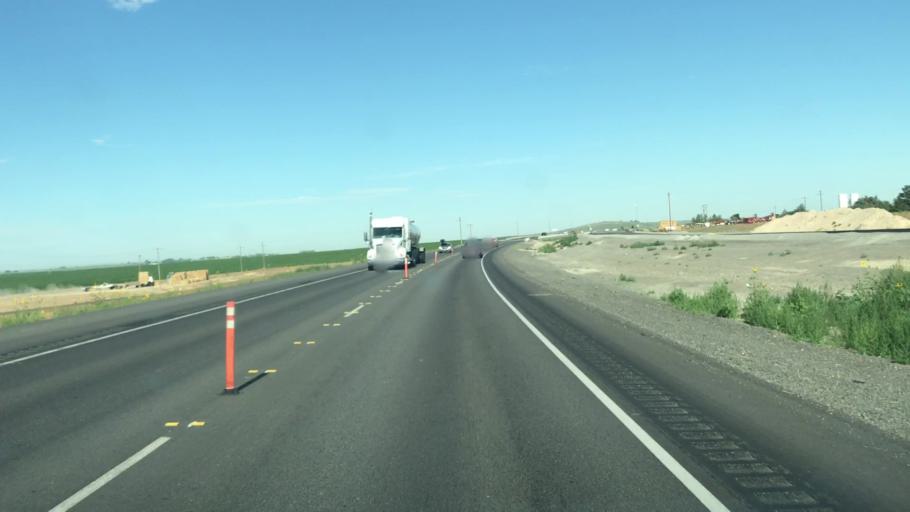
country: US
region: Idaho
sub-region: Twin Falls County
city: Hansen
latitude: 42.5741
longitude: -114.1443
